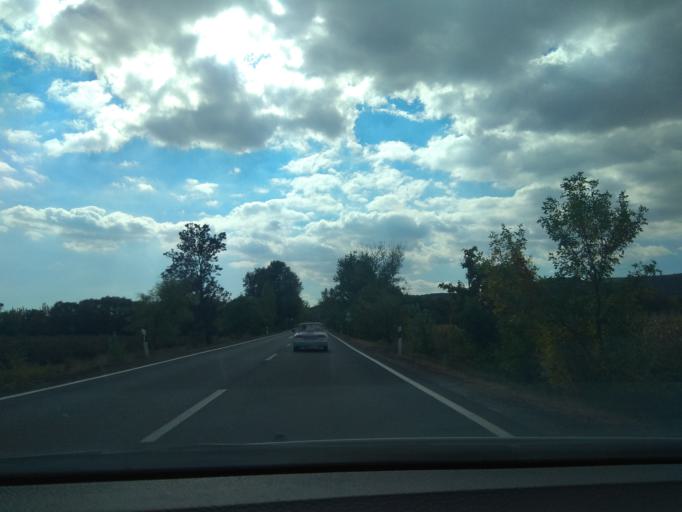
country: HU
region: Borsod-Abauj-Zemplen
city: Olaszliszka
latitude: 48.2264
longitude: 21.3999
